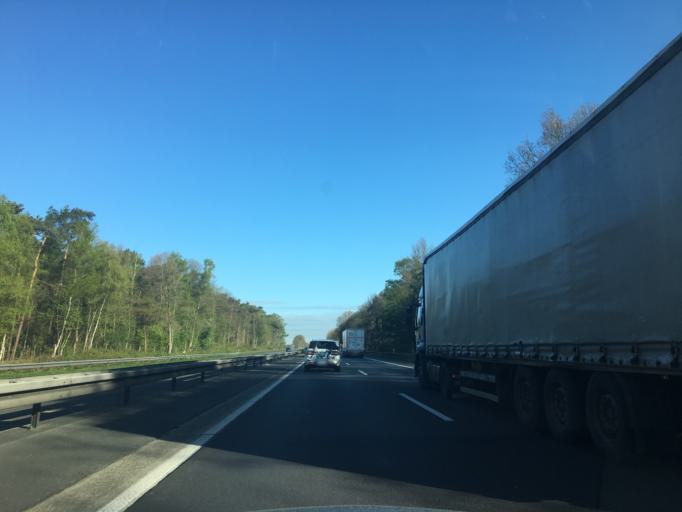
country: DE
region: North Rhine-Westphalia
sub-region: Regierungsbezirk Dusseldorf
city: Hunxe
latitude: 51.6555
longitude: 6.7320
